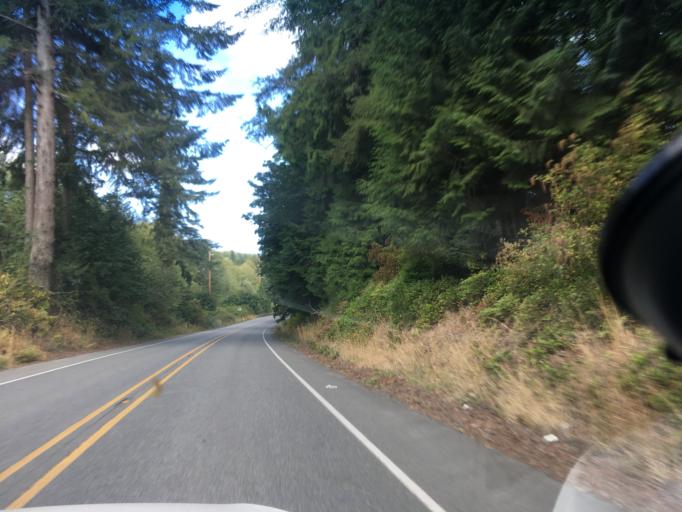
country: US
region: Washington
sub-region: Kitsap County
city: Lofall
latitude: 47.8401
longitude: -122.5873
